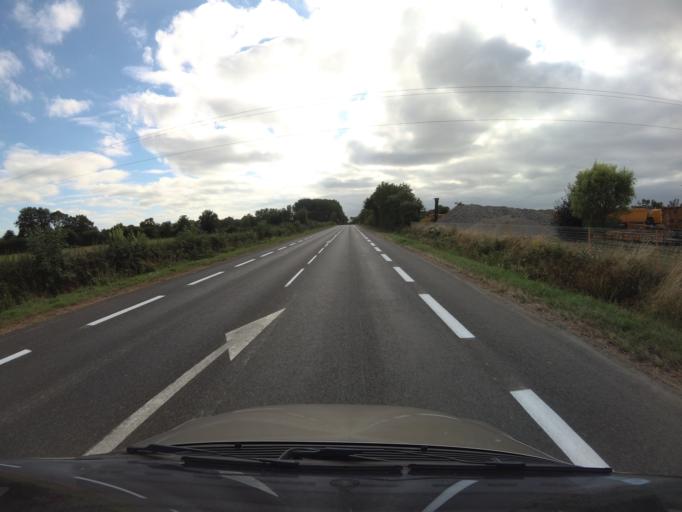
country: FR
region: Pays de la Loire
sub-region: Departement de Maine-et-Loire
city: Vezins
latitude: 47.1169
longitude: -0.7223
